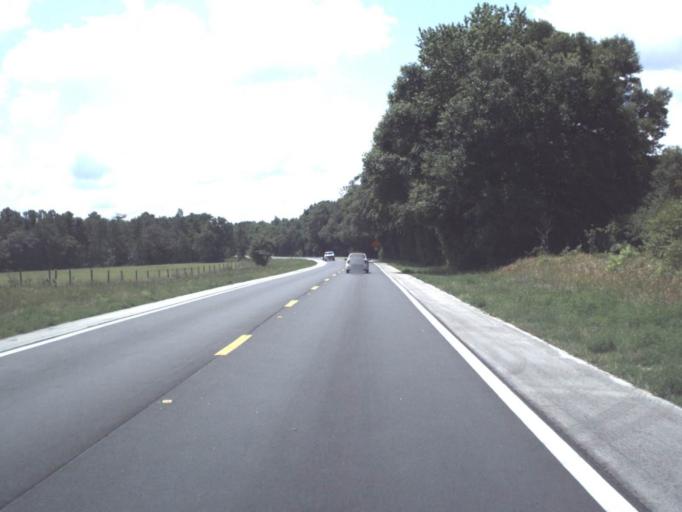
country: US
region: Florida
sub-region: Putnam County
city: Palatka
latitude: 29.5299
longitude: -81.6413
